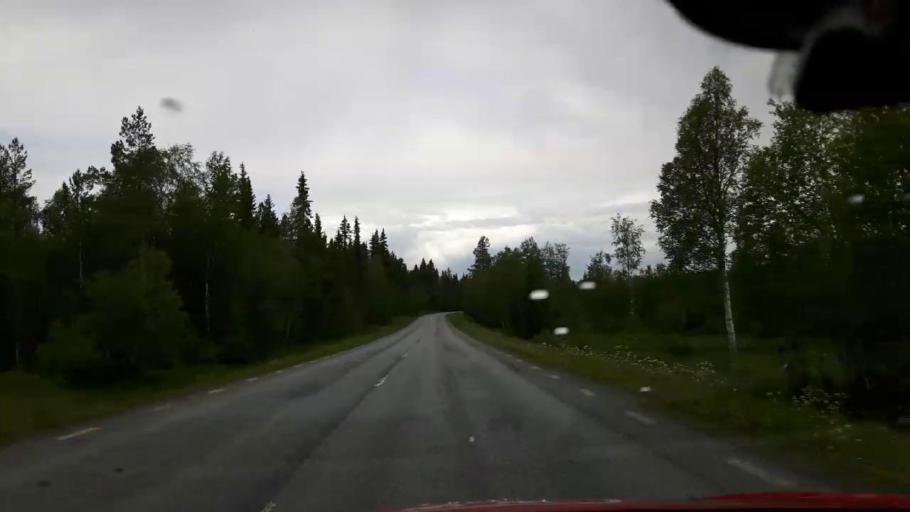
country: SE
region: Jaemtland
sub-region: Krokoms Kommun
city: Krokom
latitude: 63.4270
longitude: 14.2135
